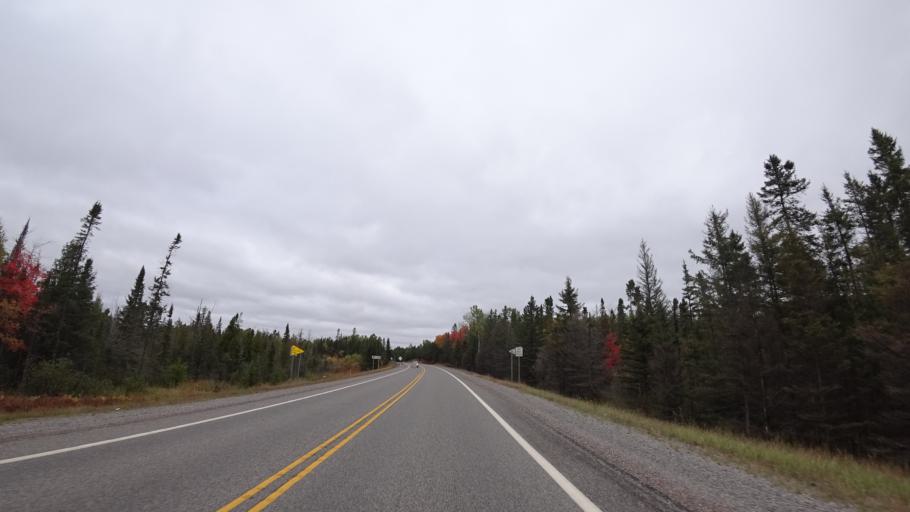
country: US
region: Michigan
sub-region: Marquette County
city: West Ishpeming
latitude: 46.4907
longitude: -87.9193
